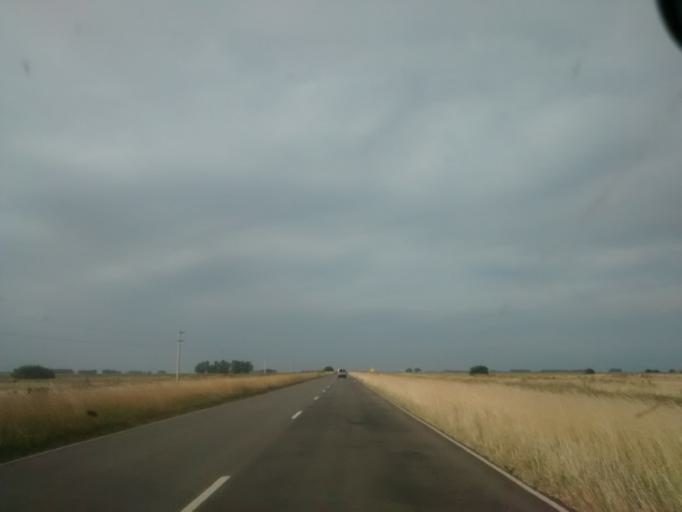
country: AR
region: Buenos Aires
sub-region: Partido de Ayacucho
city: Ayacucho
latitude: -36.8132
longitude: -58.5659
